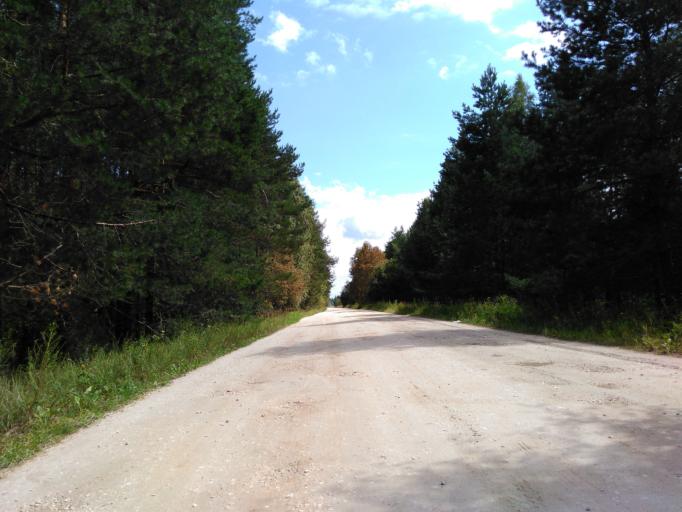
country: RU
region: Vladimir
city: Krasnyy Oktyabr'
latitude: 56.0040
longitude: 38.8398
